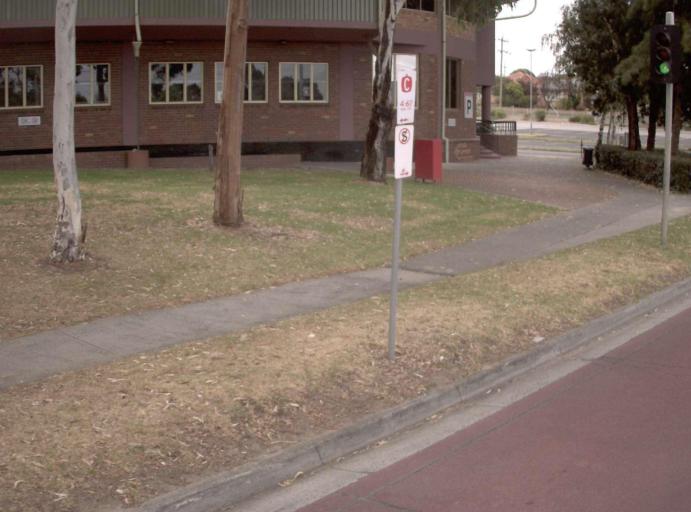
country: AU
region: Victoria
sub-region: Greater Dandenong
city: Dandenong North
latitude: -37.9752
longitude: 145.2226
